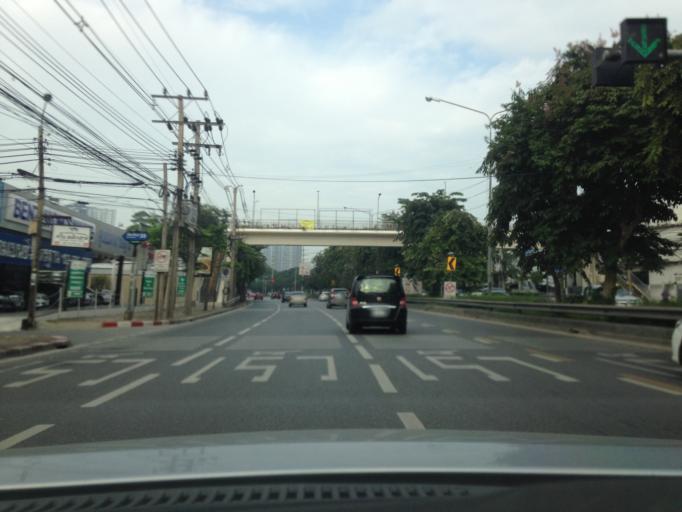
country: TH
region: Bangkok
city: Bang Sue
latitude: 13.8307
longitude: 100.5342
